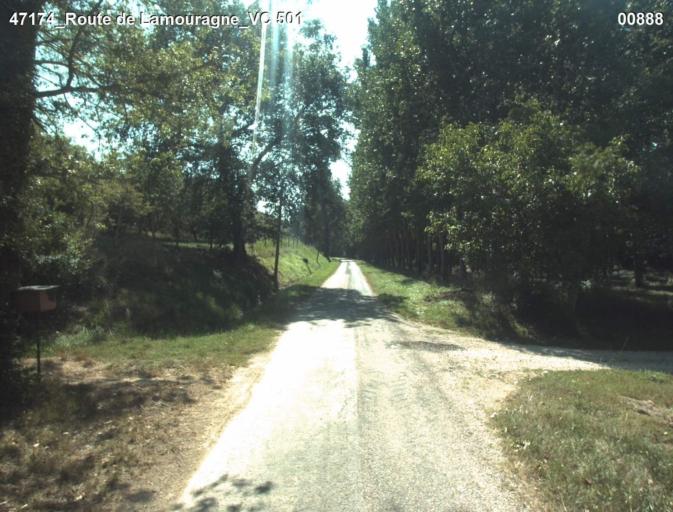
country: FR
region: Midi-Pyrenees
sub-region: Departement du Gers
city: Condom
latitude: 44.0399
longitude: 0.3872
